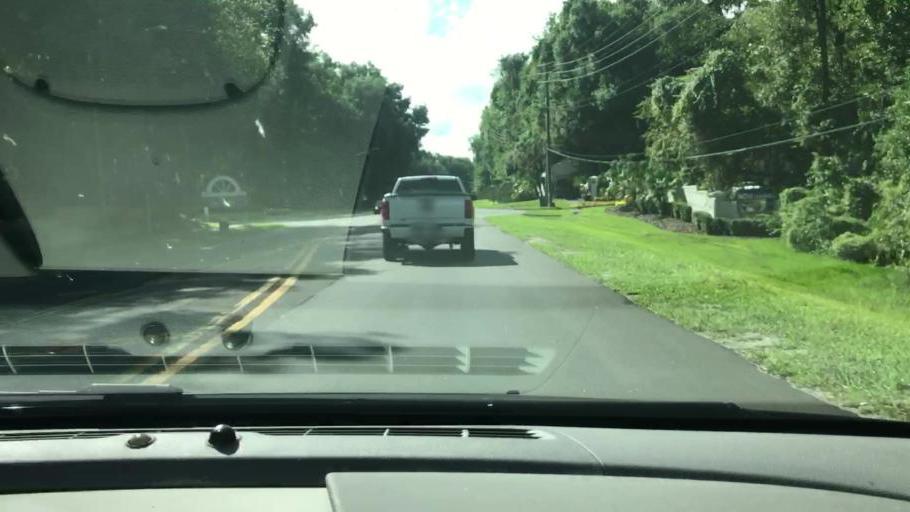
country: US
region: Florida
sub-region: Alachua County
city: Gainesville
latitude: 29.6471
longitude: -82.4012
